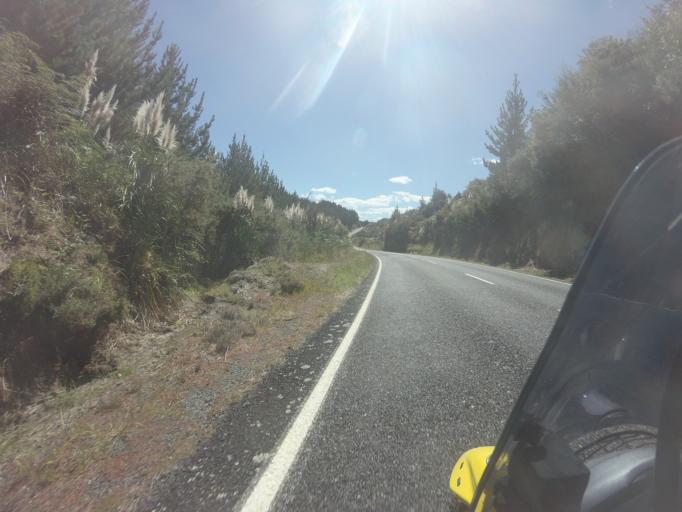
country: NZ
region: Bay of Plenty
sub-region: Kawerau District
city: Kawerau
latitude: -38.2814
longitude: 176.8164
